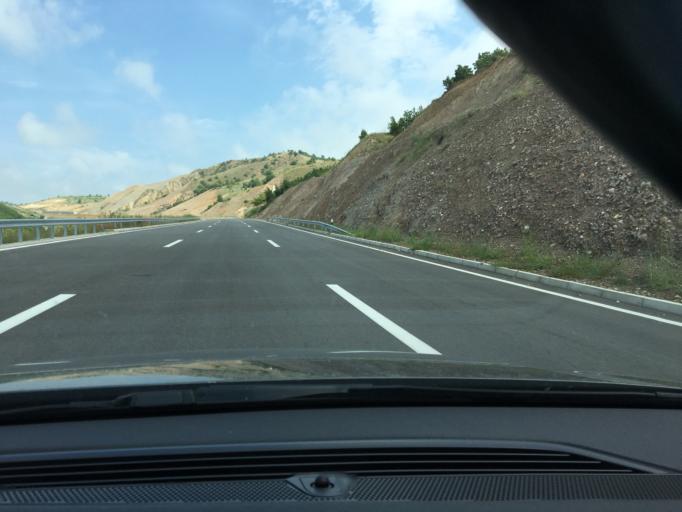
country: MK
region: Petrovec
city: Sredno Konjare
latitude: 41.9672
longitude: 21.7007
